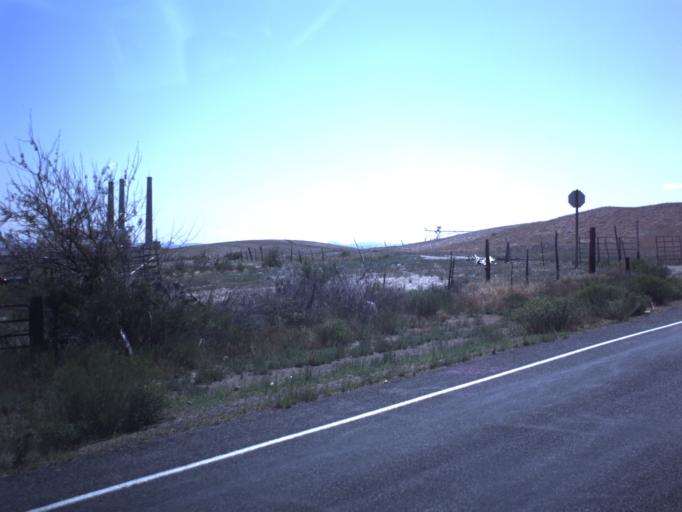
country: US
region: Utah
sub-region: Emery County
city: Castle Dale
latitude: 39.1850
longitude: -111.0477
